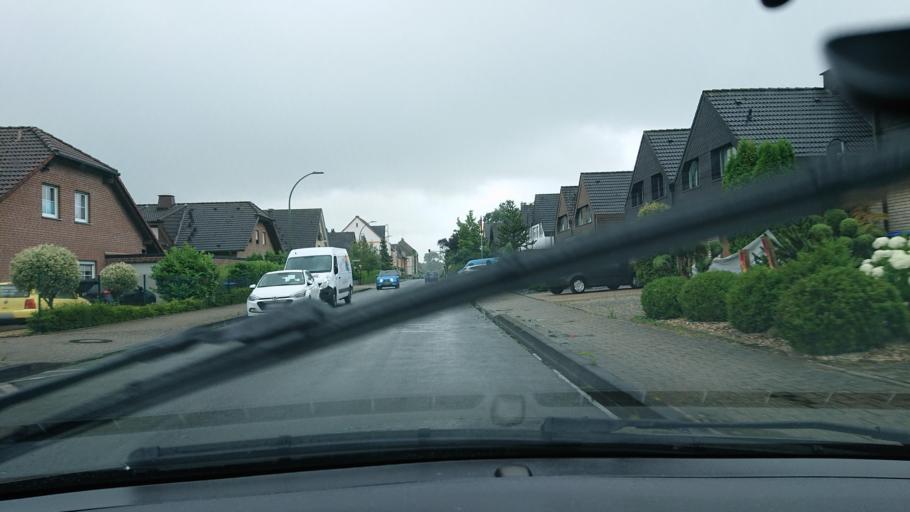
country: DE
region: North Rhine-Westphalia
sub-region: Regierungsbezirk Arnsberg
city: Hamm
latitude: 51.6856
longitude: 7.8918
